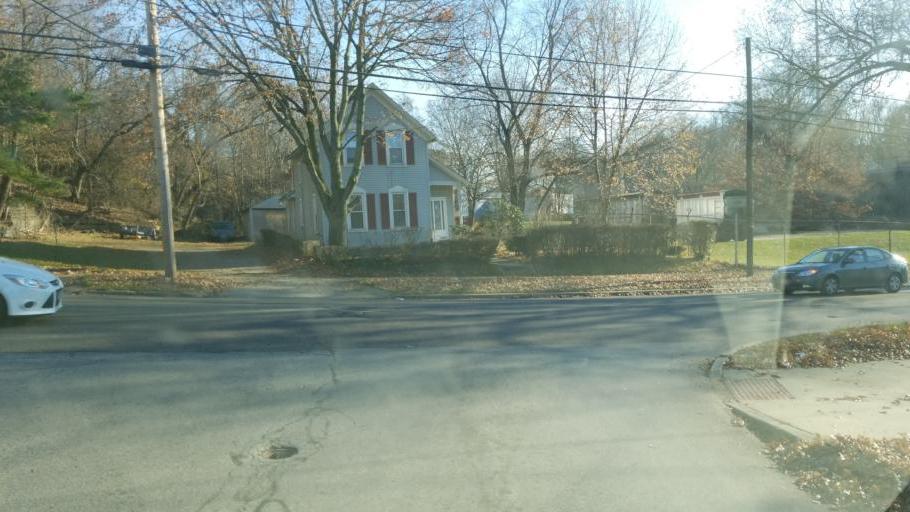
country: US
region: Ohio
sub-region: Summit County
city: Akron
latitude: 41.0748
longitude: -81.4810
